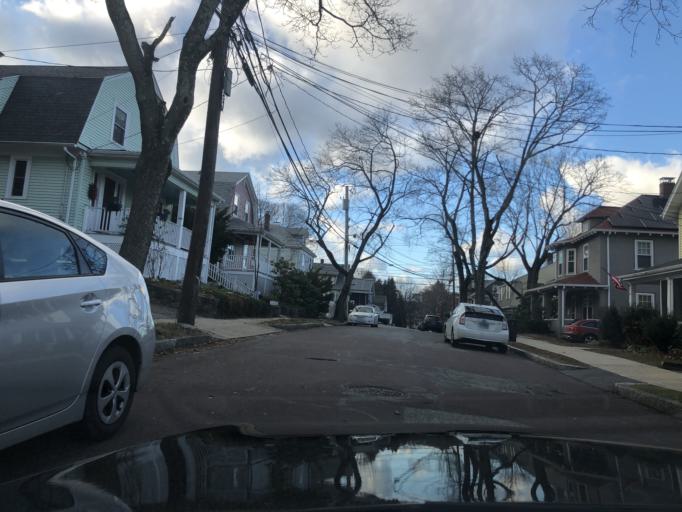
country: US
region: Massachusetts
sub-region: Middlesex County
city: Arlington
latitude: 42.4167
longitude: -71.1651
